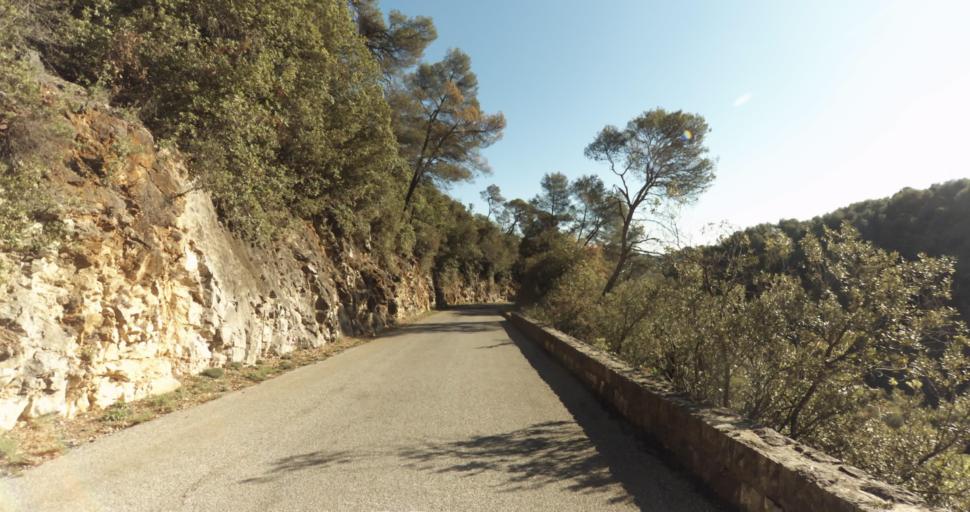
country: FR
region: Provence-Alpes-Cote d'Azur
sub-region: Departement des Alpes-Maritimes
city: Vence
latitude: 43.7131
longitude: 7.1165
